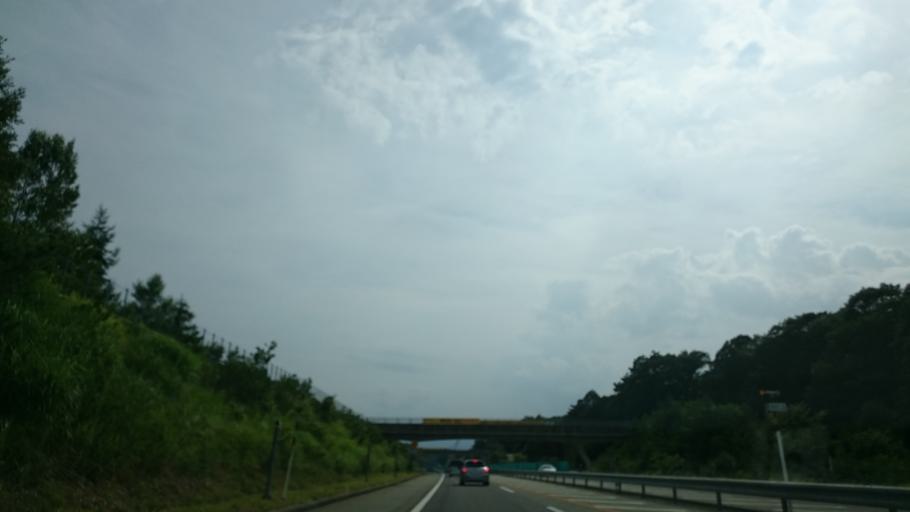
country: JP
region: Gifu
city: Gujo
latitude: 35.9832
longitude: 136.9040
